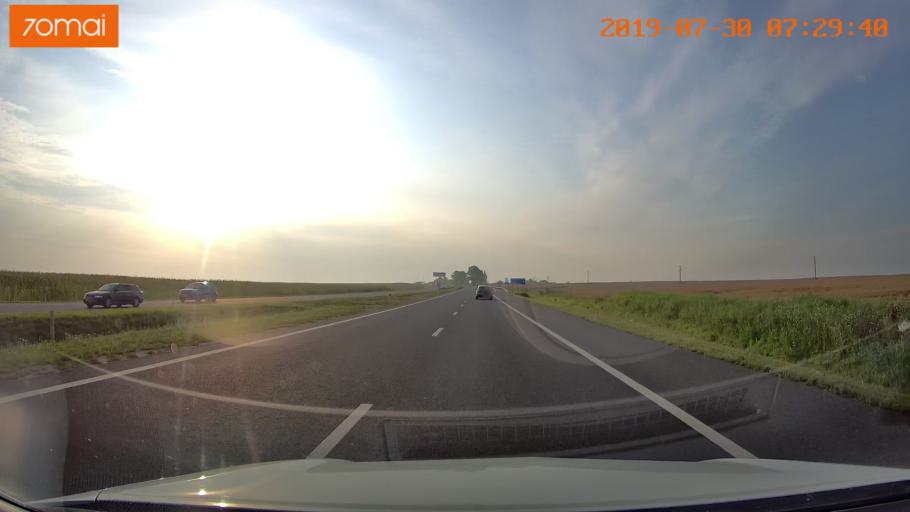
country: RU
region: Kaliningrad
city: Gvardeysk
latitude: 54.6712
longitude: 20.9454
